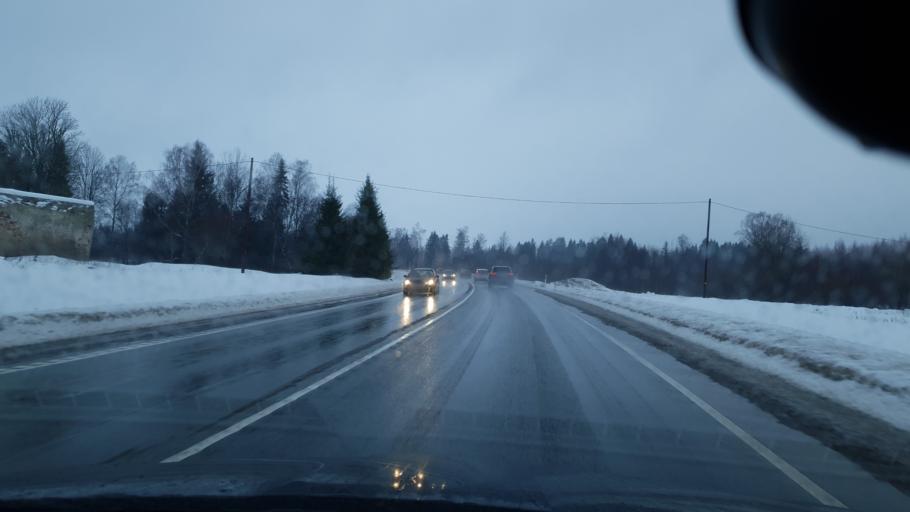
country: EE
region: Harju
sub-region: Anija vald
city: Kehra
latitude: 59.1633
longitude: 25.2827
